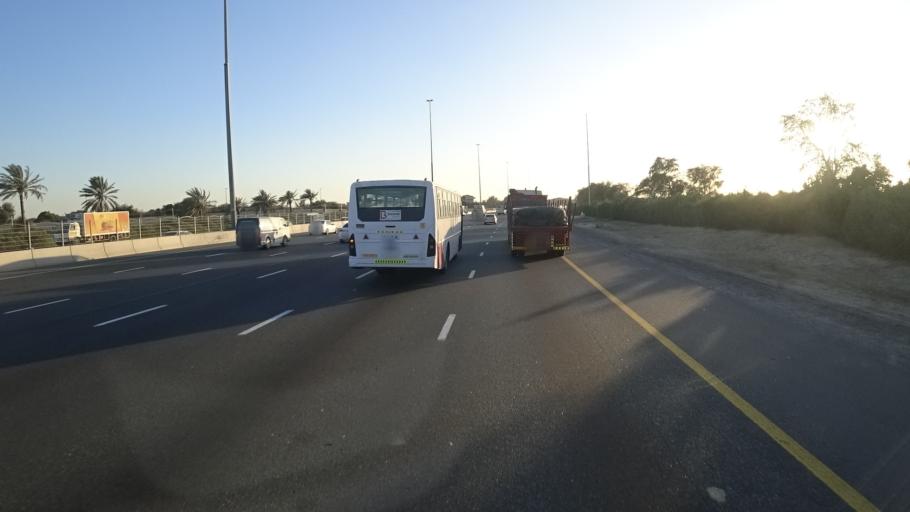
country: AE
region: Dubai
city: Dubai
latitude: 25.0649
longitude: 55.2942
